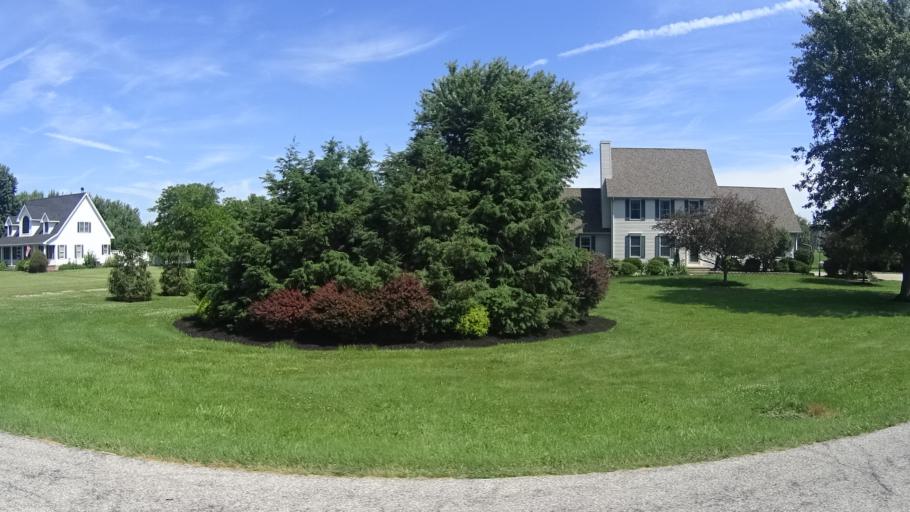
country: US
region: Ohio
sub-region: Huron County
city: Wakeman
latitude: 41.3321
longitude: -82.4519
